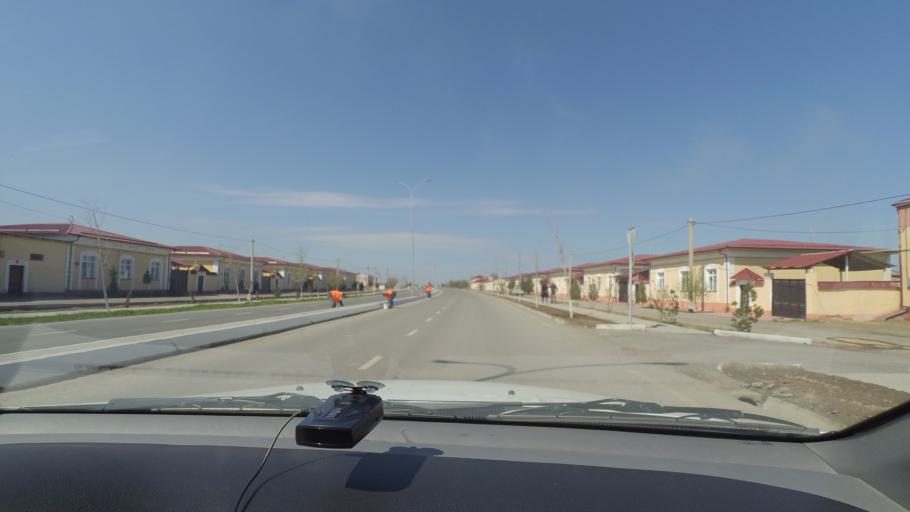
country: UZ
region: Bukhara
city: Kogon
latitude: 39.8026
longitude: 64.5220
